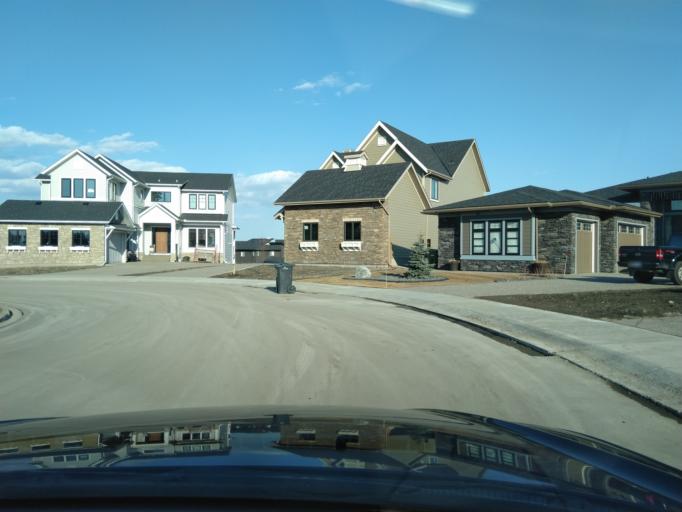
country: CA
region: Alberta
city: Cochrane
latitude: 51.1112
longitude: -114.4016
